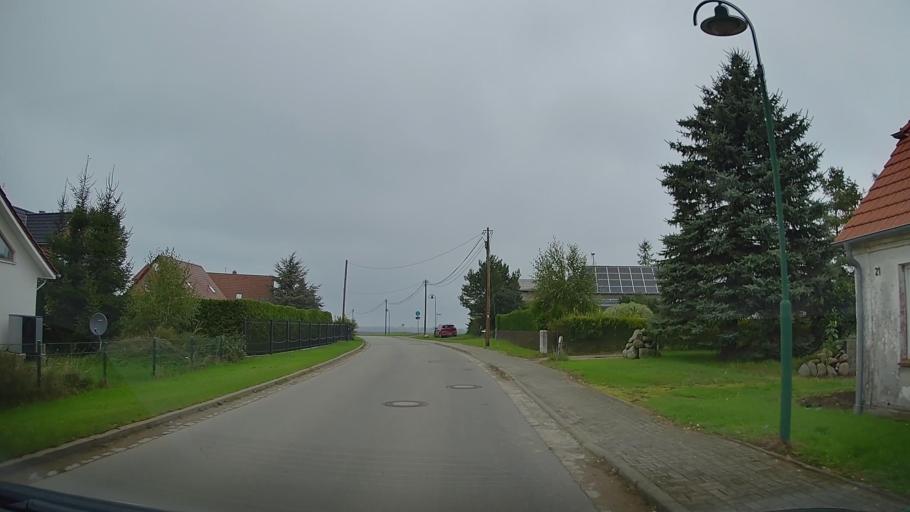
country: DE
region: Mecklenburg-Vorpommern
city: Neubukow
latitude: 54.0409
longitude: 11.6214
